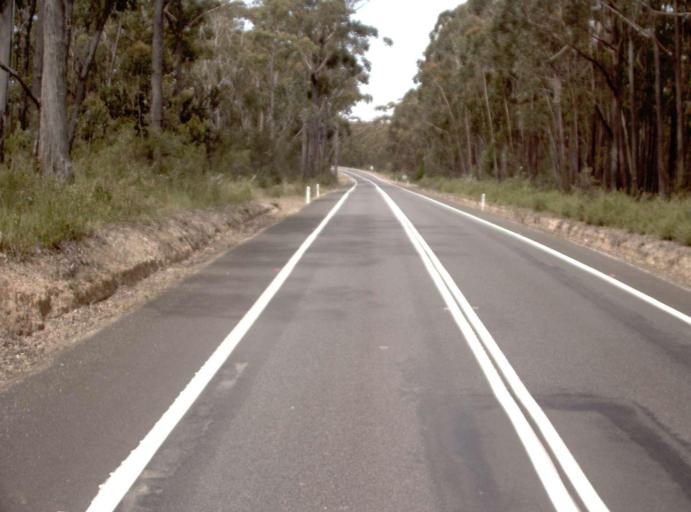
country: AU
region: New South Wales
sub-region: Bega Valley
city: Eden
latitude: -37.5081
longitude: 149.5228
